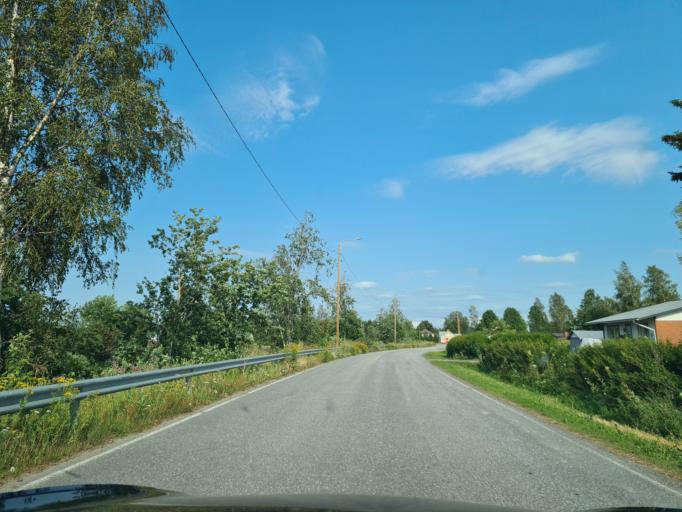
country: FI
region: Ostrobothnia
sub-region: Vaasa
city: Ristinummi
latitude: 63.0320
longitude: 21.8533
